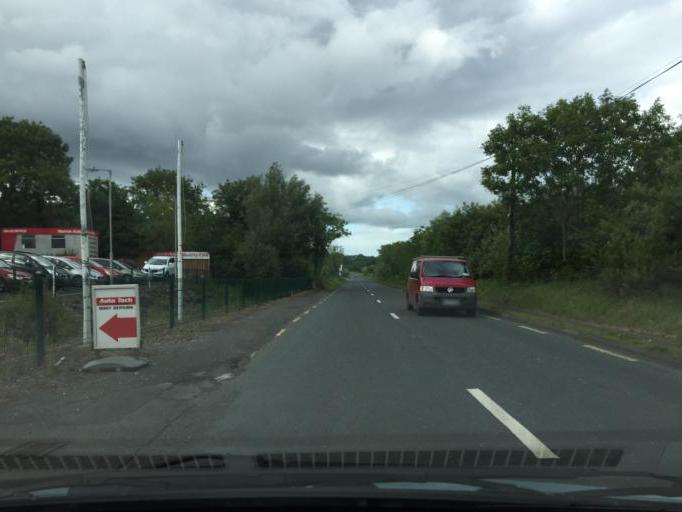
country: IE
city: Ballisodare
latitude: 54.2288
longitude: -8.4902
